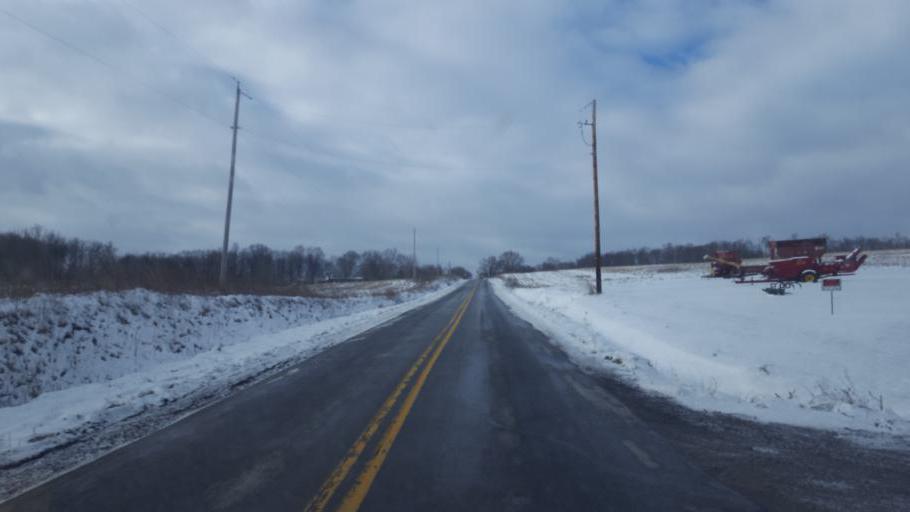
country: US
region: Pennsylvania
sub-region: Mercer County
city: Mercer
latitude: 41.1770
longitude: -80.2463
